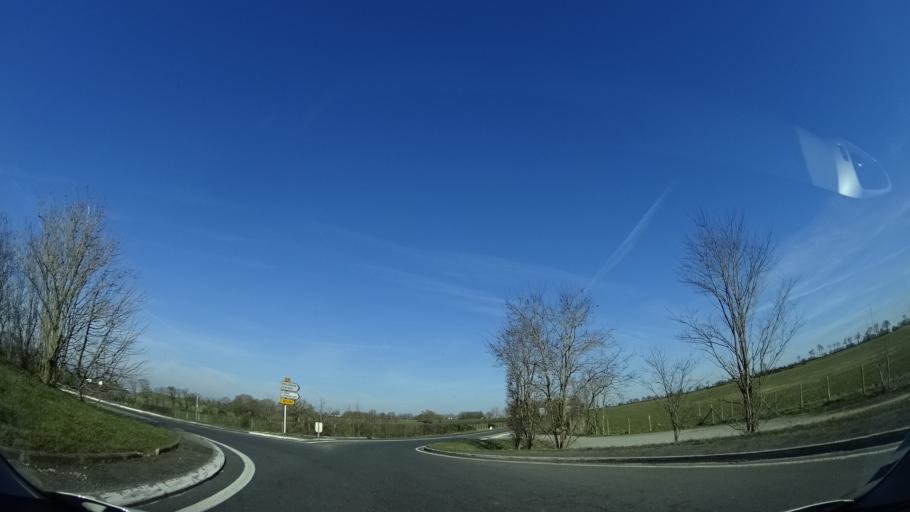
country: FR
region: Poitou-Charentes
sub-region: Departement des Deux-Sevres
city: Saint-Pierre-des-Echaubrognes
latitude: 46.9424
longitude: -0.7536
